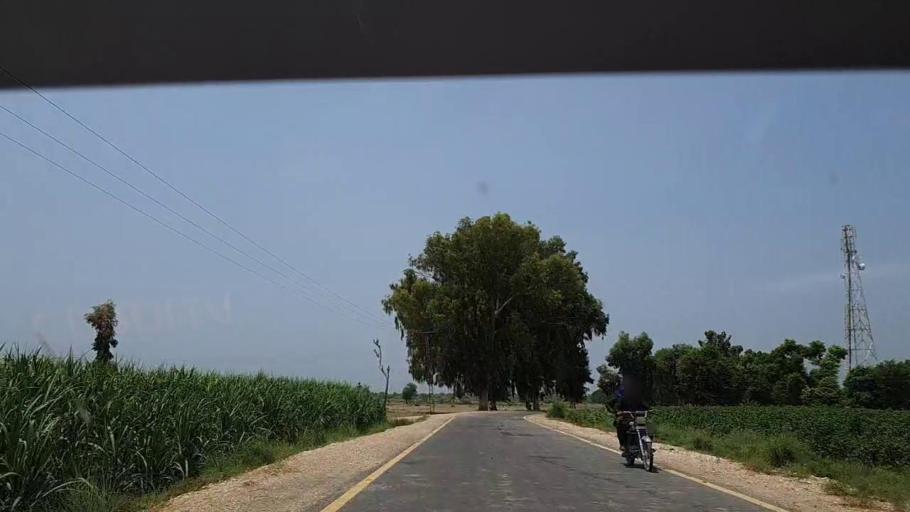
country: PK
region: Sindh
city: Adilpur
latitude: 27.8739
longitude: 69.2779
